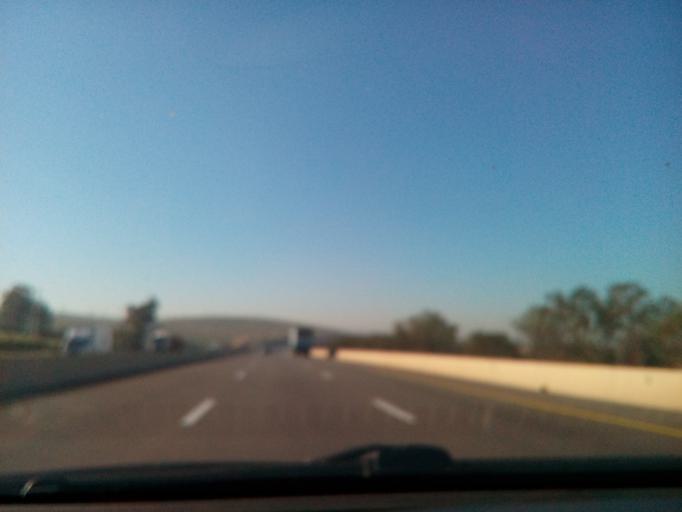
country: DZ
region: Chlef
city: Oued Sly
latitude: 36.0718
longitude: 1.1708
